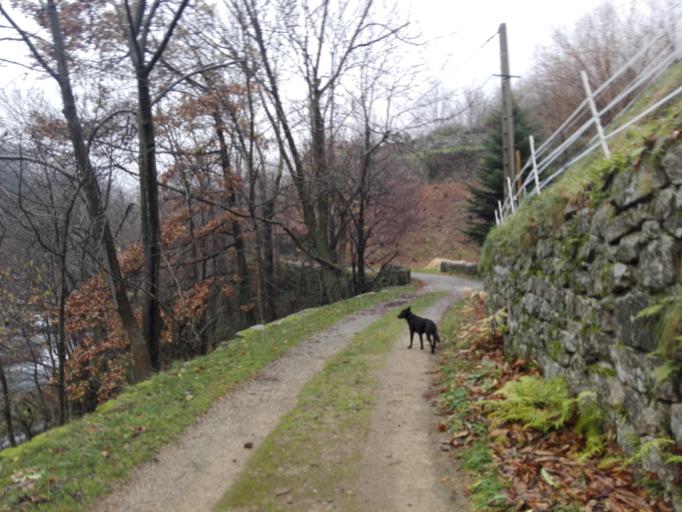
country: FR
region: Rhone-Alpes
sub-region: Departement de l'Ardeche
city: Thueyts
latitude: 44.7443
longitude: 4.2497
